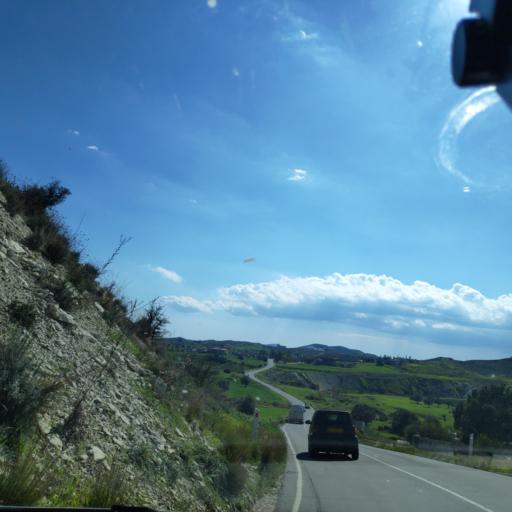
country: CY
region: Lefkosia
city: Tseri
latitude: 35.0298
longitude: 33.3277
